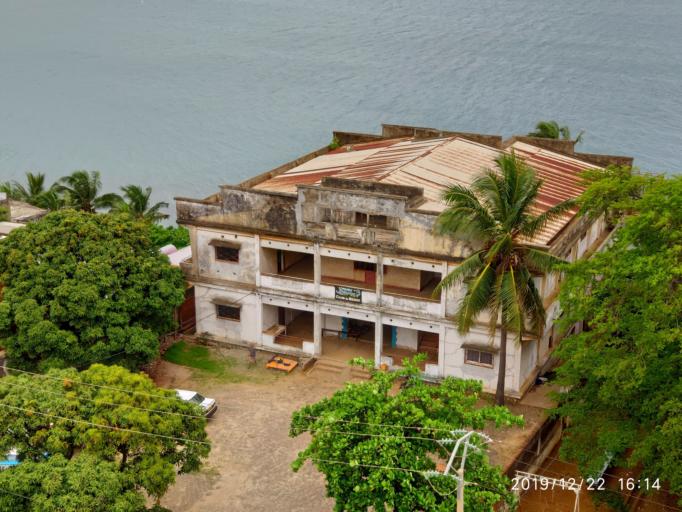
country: MG
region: Diana
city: Antsiranana
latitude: -12.2688
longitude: 49.2918
